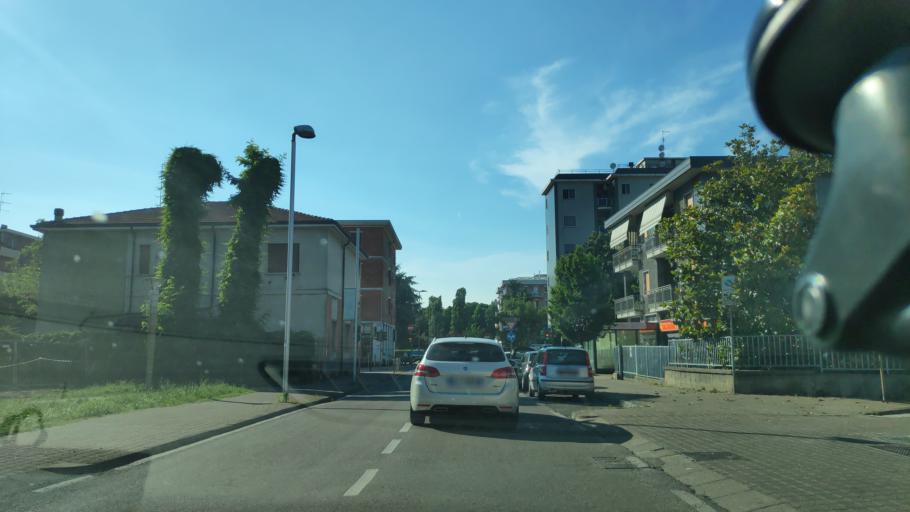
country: IT
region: Lombardy
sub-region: Citta metropolitana di Milano
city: Rozzano
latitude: 45.3761
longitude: 9.1453
